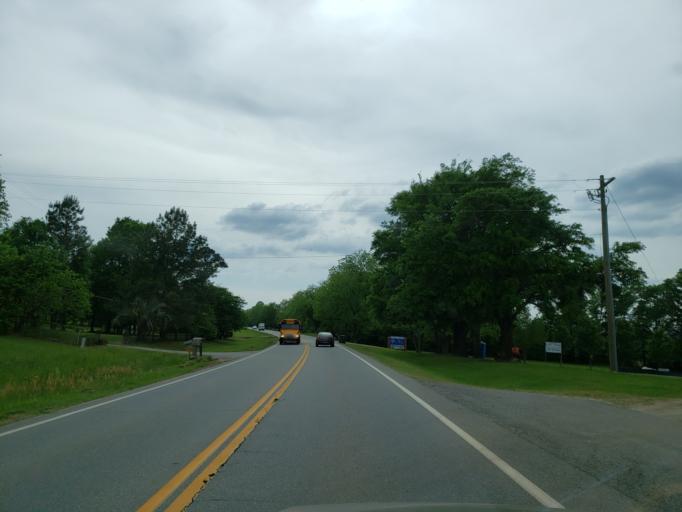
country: US
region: Georgia
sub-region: Houston County
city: Perry
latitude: 32.4468
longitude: -83.7676
